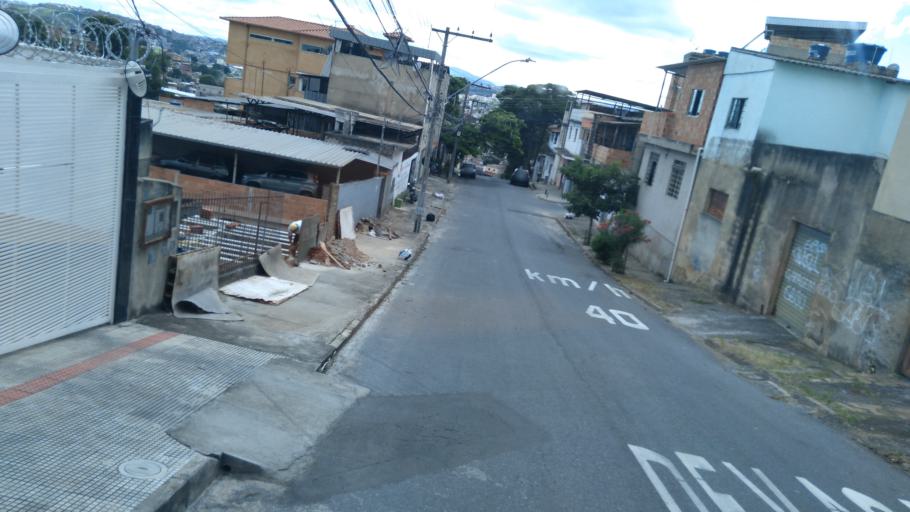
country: BR
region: Minas Gerais
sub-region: Belo Horizonte
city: Belo Horizonte
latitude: -19.8617
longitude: -43.9142
